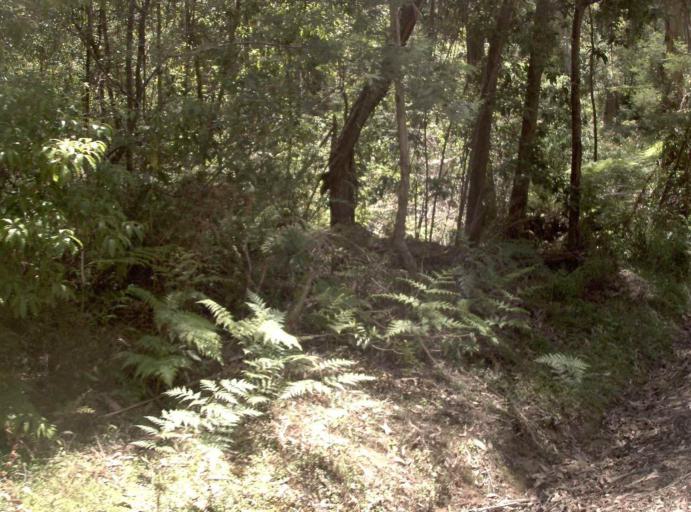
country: AU
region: New South Wales
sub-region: Bombala
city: Bombala
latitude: -37.4881
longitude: 148.9276
